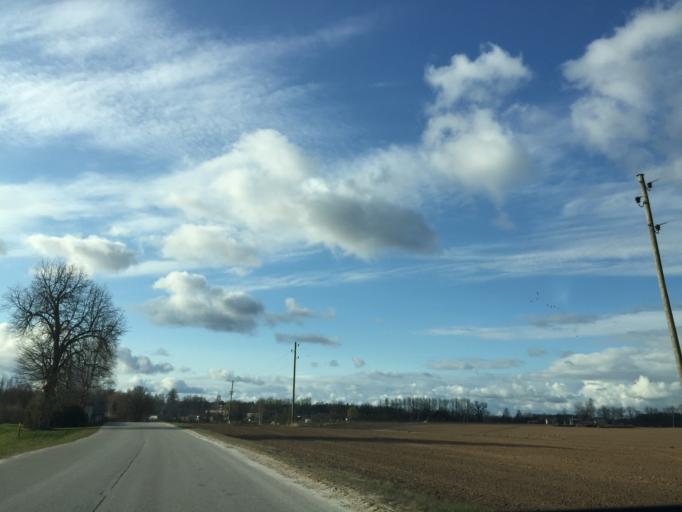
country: LV
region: Burtnieki
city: Matisi
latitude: 57.6323
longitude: 25.0539
